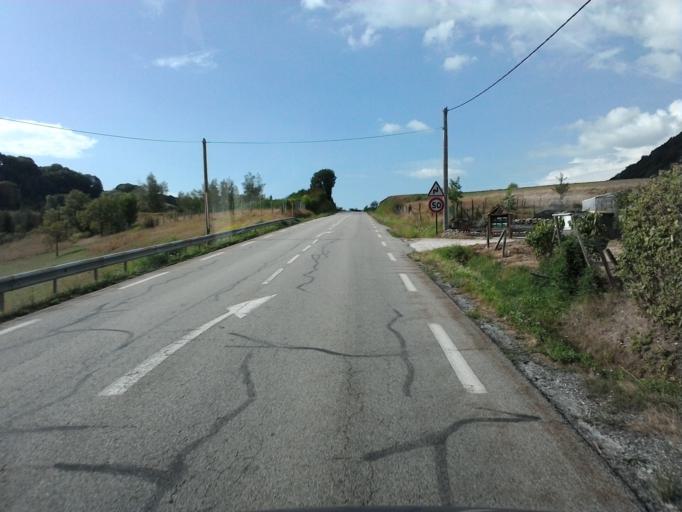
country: FR
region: Rhone-Alpes
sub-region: Departement de l'Isere
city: Bilieu
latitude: 45.4346
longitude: 5.5652
